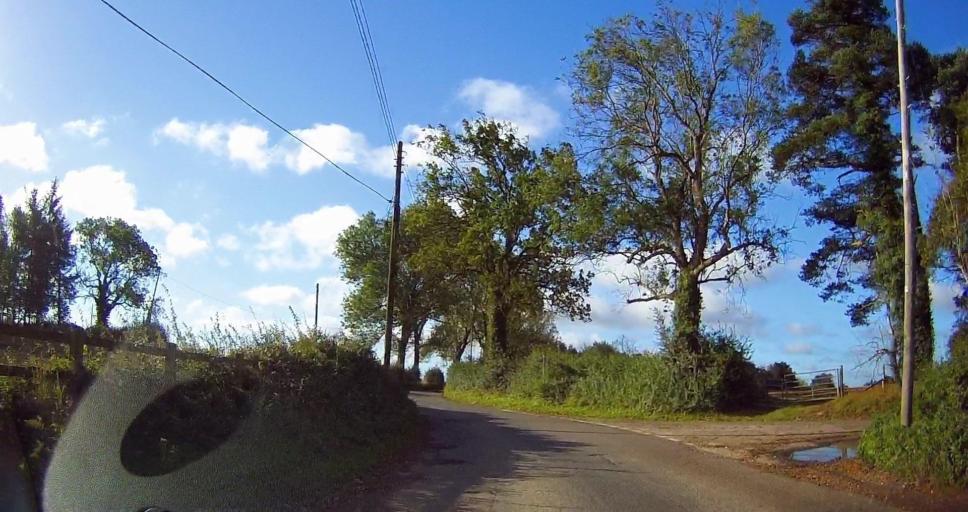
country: GB
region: England
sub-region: Kent
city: Borough Green
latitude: 51.3190
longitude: 0.2772
